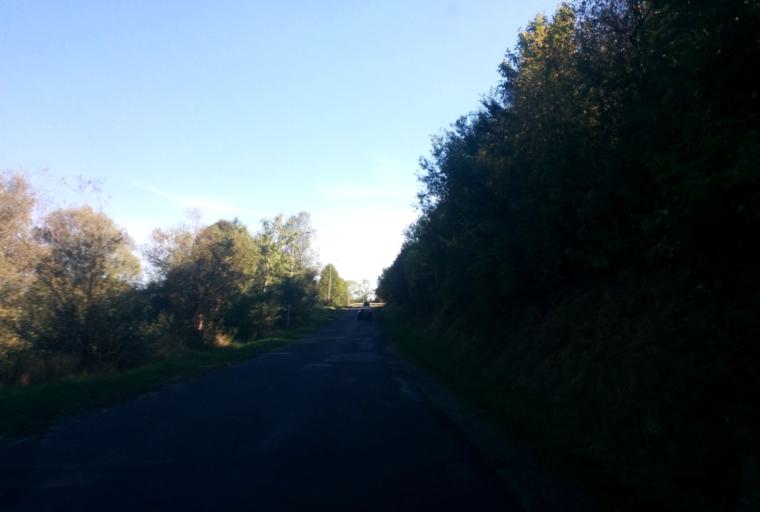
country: PL
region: Subcarpathian Voivodeship
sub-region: Powiat leski
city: Polanczyk
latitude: 49.3320
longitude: 22.4165
